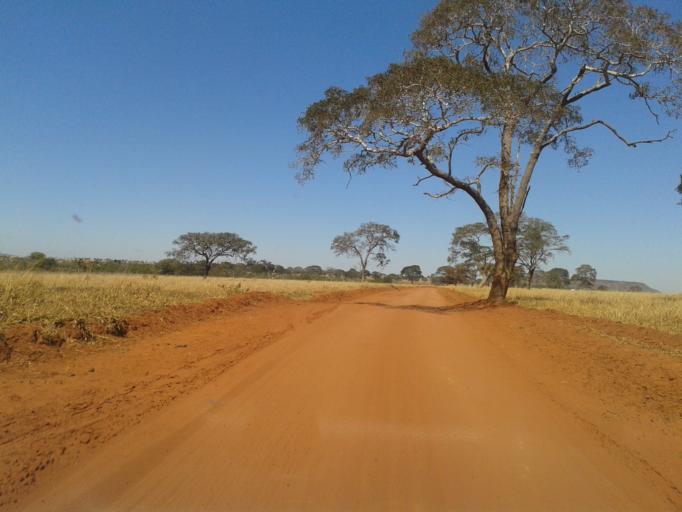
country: BR
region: Minas Gerais
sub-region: Santa Vitoria
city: Santa Vitoria
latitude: -19.1608
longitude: -50.1562
